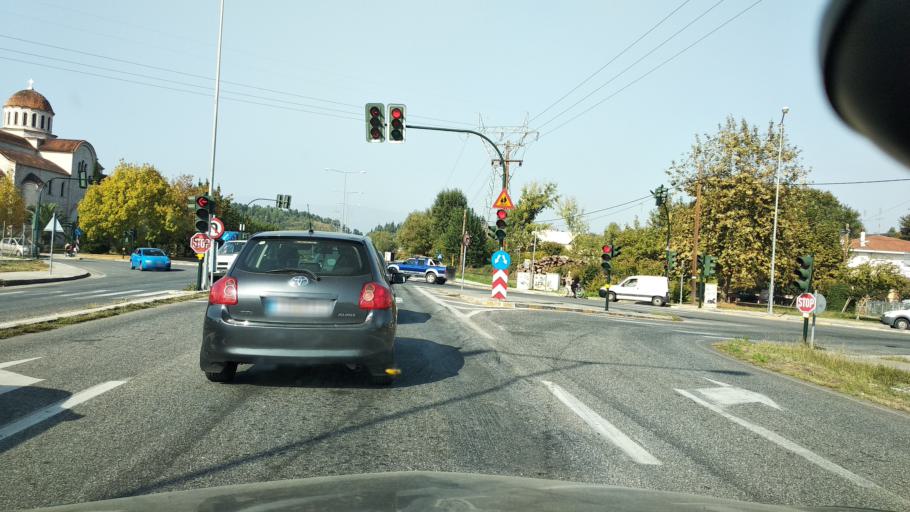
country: GR
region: Thessaly
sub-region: Trikala
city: Trikala
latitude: 39.5658
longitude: 21.7776
